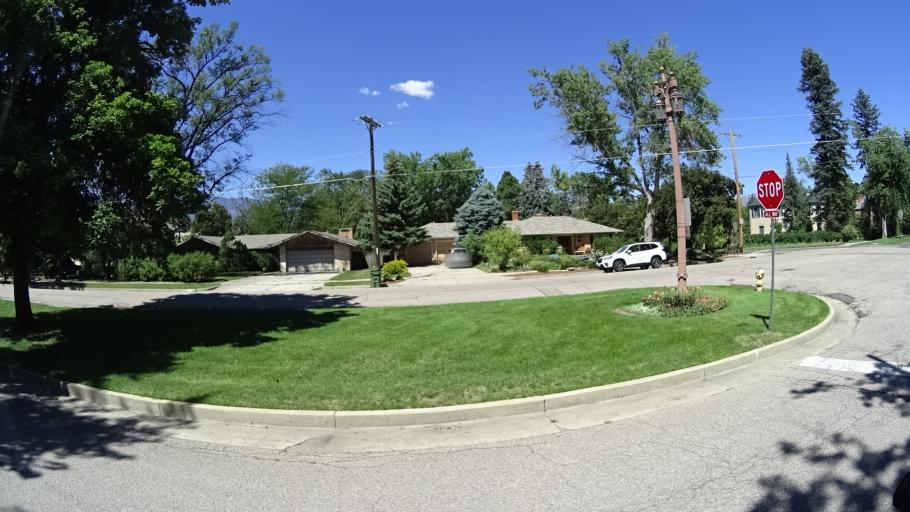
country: US
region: Colorado
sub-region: El Paso County
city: Colorado Springs
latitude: 38.8536
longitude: -104.8260
